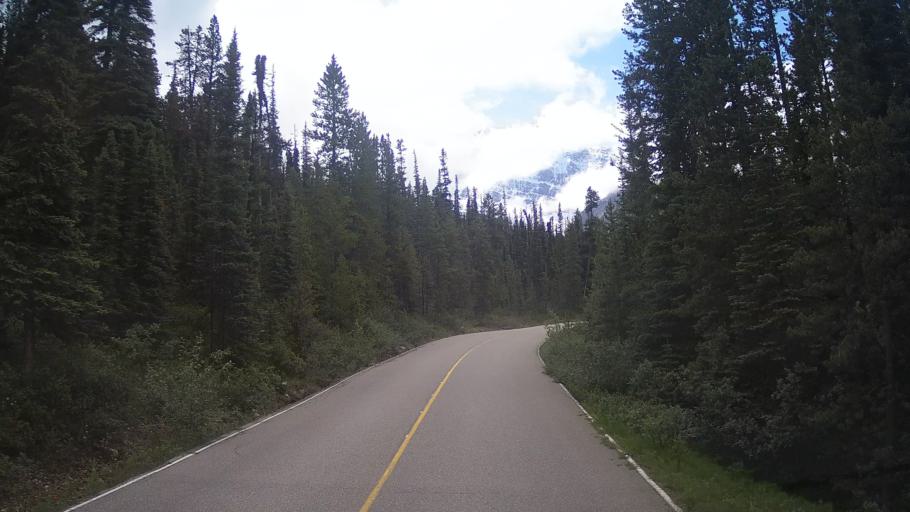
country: CA
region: Alberta
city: Jasper Park Lodge
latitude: 52.7211
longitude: -118.0517
